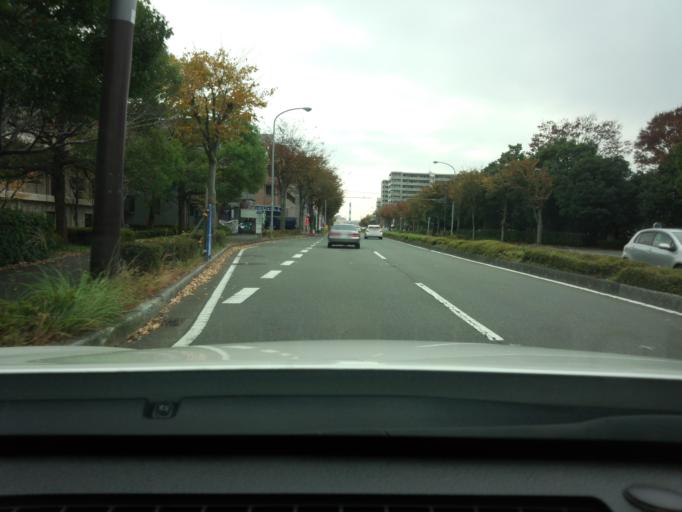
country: JP
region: Tokyo
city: Chofugaoka
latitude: 35.5591
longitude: 139.5789
